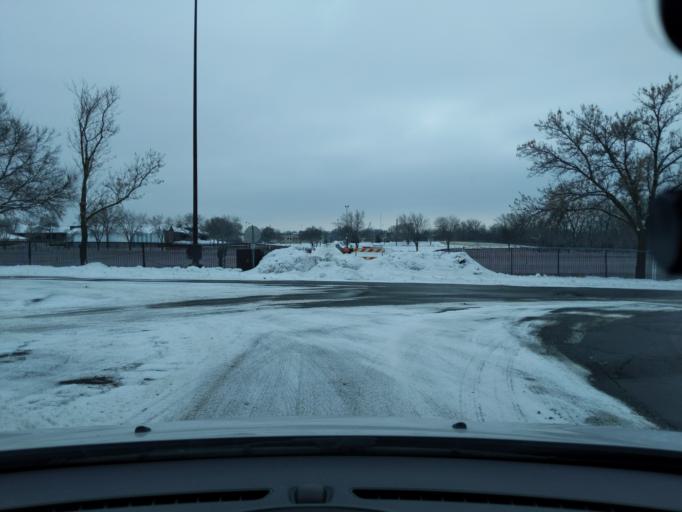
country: US
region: Minnesota
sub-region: Ramsey County
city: Falcon Heights
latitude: 44.9809
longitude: -93.1795
